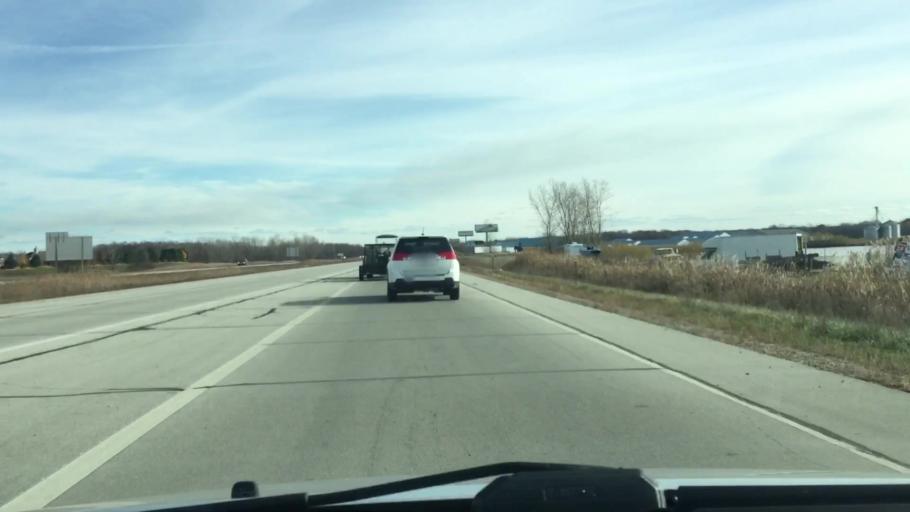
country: US
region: Wisconsin
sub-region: Brown County
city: Pulaski
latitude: 44.5950
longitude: -88.2153
